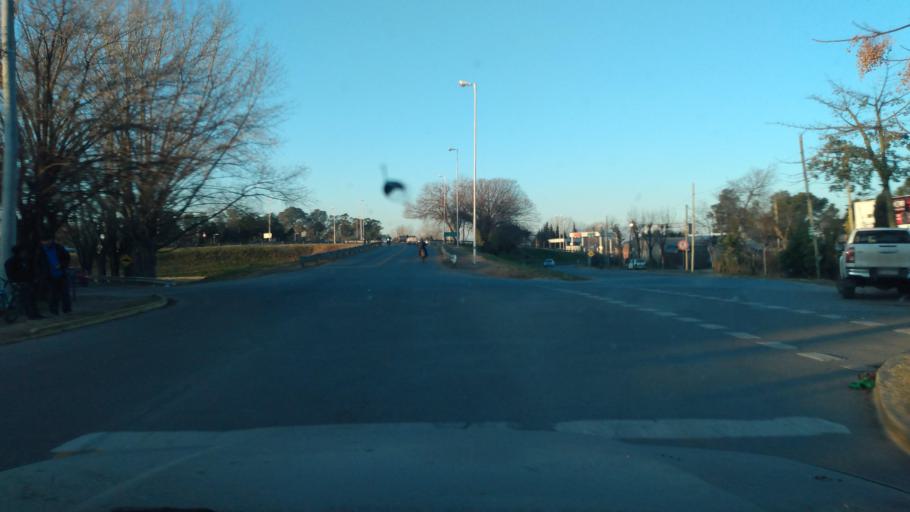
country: AR
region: Buenos Aires
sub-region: Partido de General Rodriguez
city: General Rodriguez
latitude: -34.5970
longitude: -58.9385
